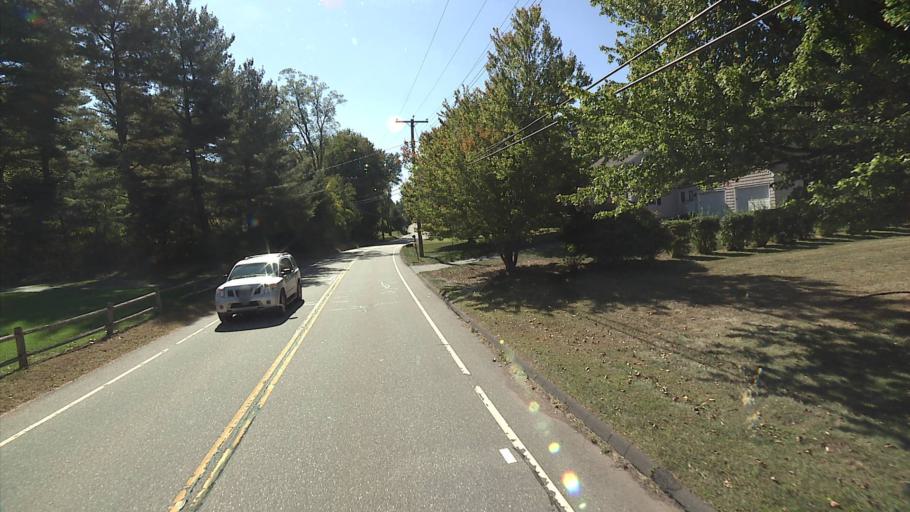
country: US
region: Connecticut
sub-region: Hartford County
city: Manchester
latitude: 41.7239
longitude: -72.5262
